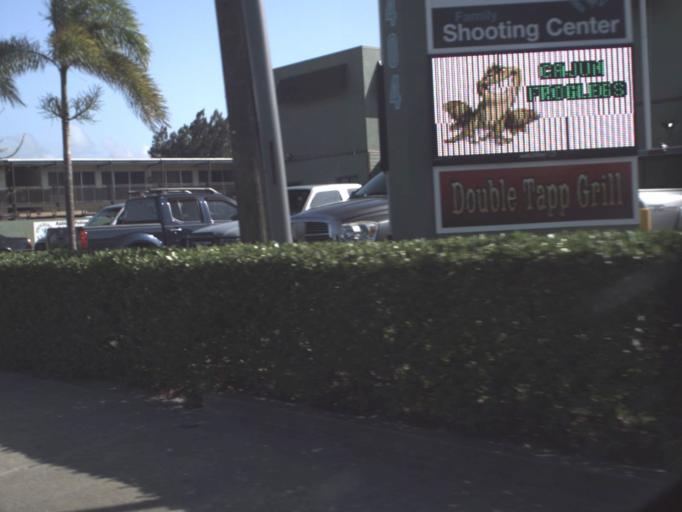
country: US
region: Florida
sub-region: Brevard County
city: Melbourne
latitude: 28.1038
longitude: -80.6152
